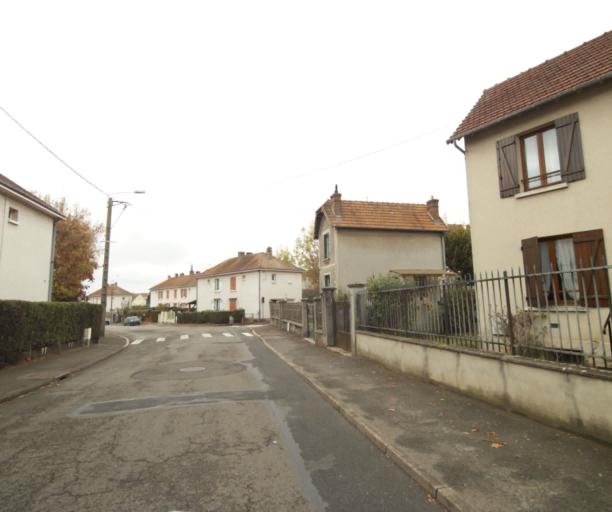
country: FR
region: Centre
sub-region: Departement d'Eure-et-Loir
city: Dreux
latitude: 48.7410
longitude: 1.3542
